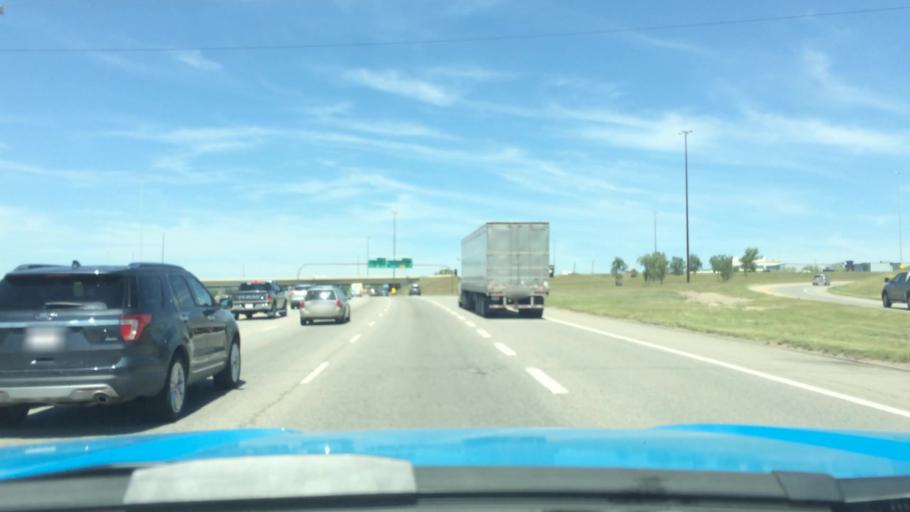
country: CA
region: Alberta
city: Calgary
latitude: 51.0930
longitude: -114.0395
